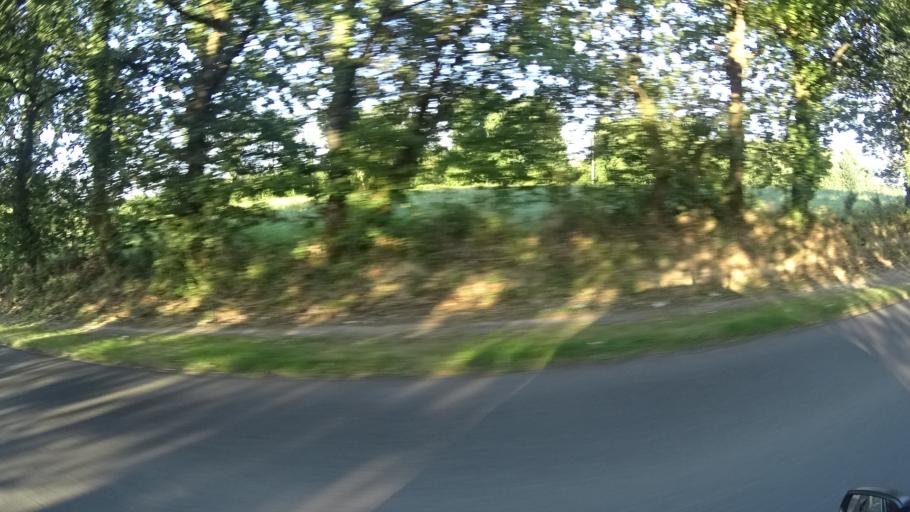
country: FR
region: Brittany
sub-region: Departement d'Ille-et-Vilaine
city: Langon
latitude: 47.7260
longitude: -1.8512
